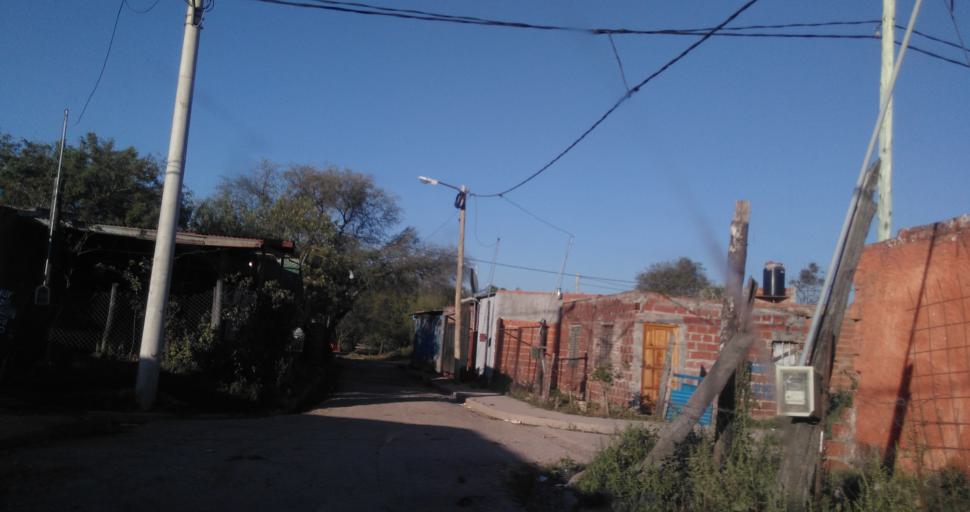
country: AR
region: Chaco
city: Resistencia
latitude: -27.4831
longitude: -58.9963
